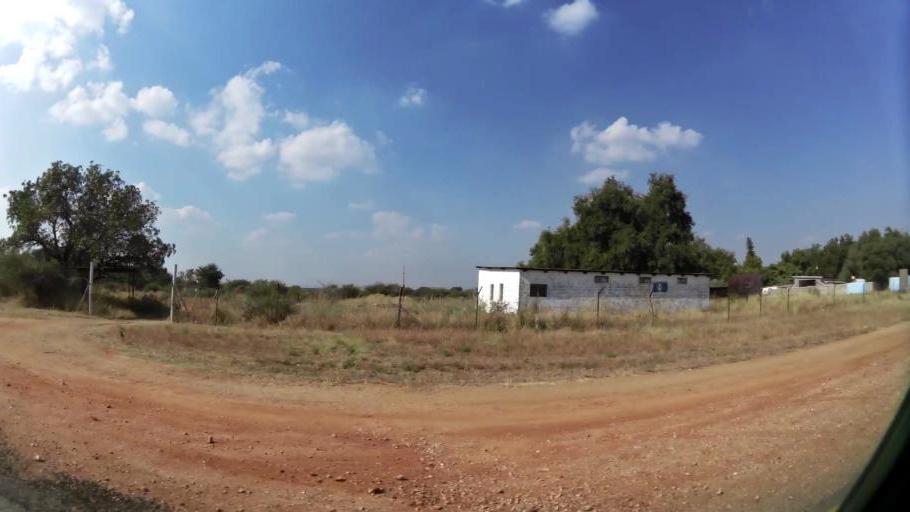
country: ZA
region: North-West
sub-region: Bojanala Platinum District Municipality
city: Rustenburg
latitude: -25.4854
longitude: 27.0861
